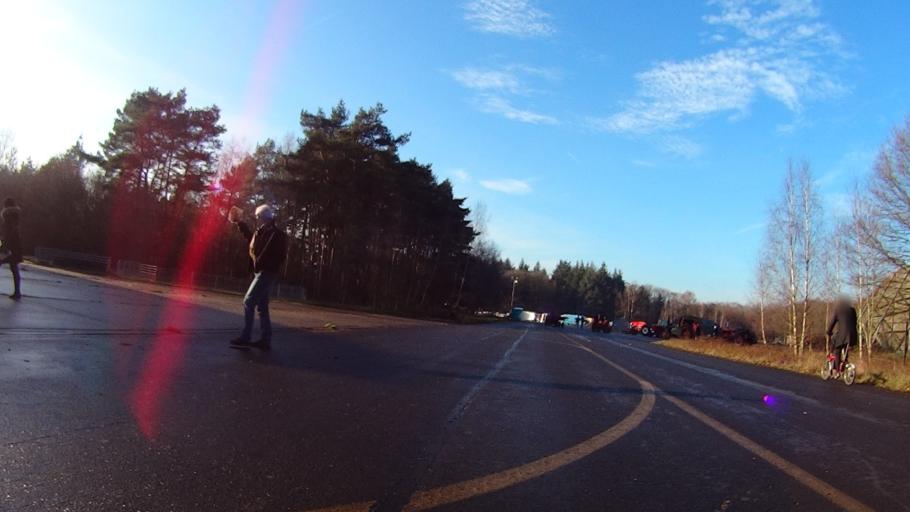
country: NL
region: Utrecht
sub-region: Gemeente Zeist
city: Zeist
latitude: 52.1301
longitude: 5.2600
